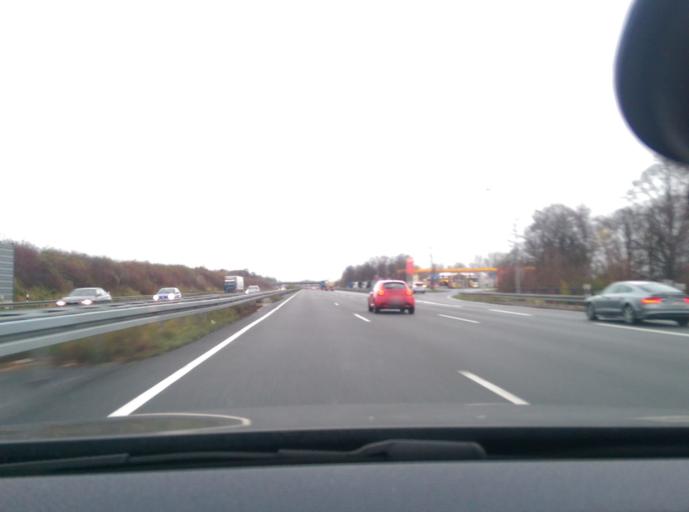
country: DE
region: Lower Saxony
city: Rosdorf
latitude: 51.4861
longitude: 9.8756
